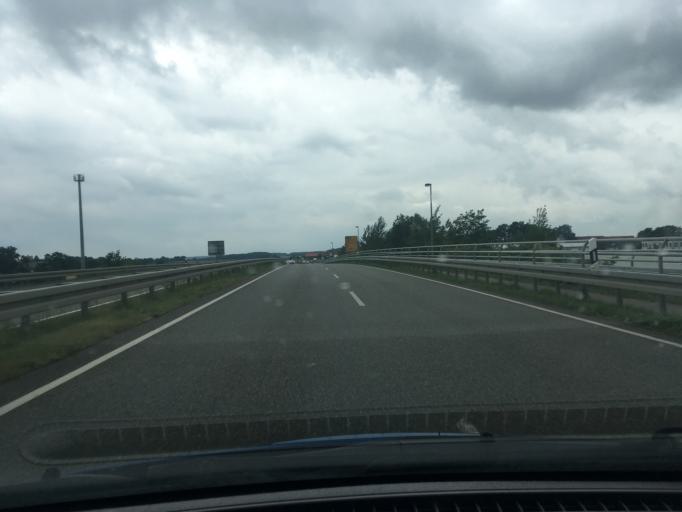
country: DE
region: Mecklenburg-Vorpommern
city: Klein Rogahn
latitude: 53.5682
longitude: 11.3728
